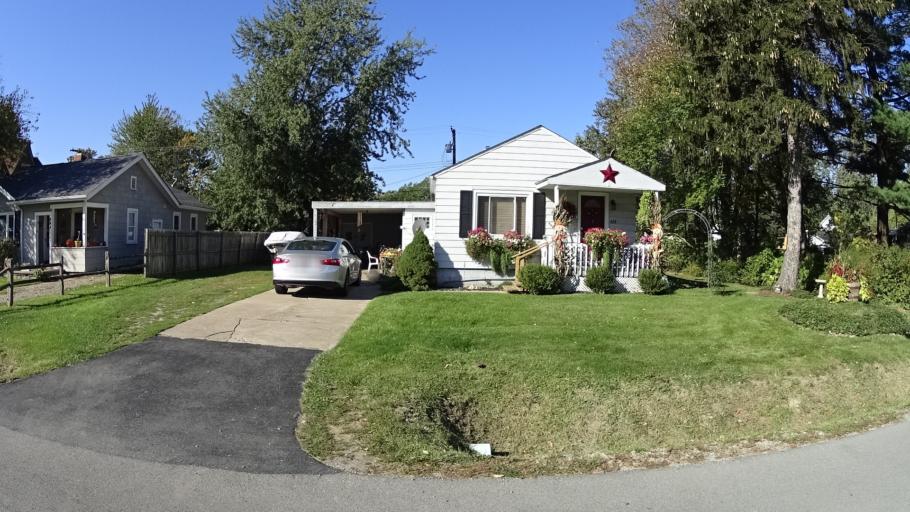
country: US
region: Ohio
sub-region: Lorain County
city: Vermilion-on-the-Lake
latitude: 41.4260
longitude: -82.3393
